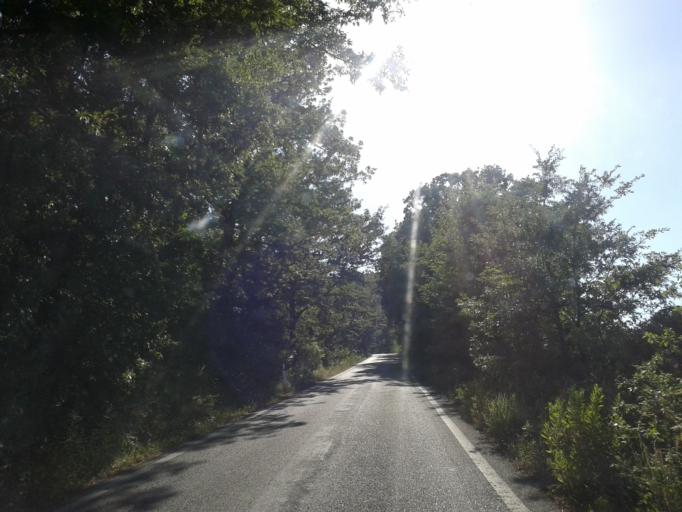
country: IT
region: Tuscany
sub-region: Province of Pisa
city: Chianni
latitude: 43.4537
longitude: 10.6299
